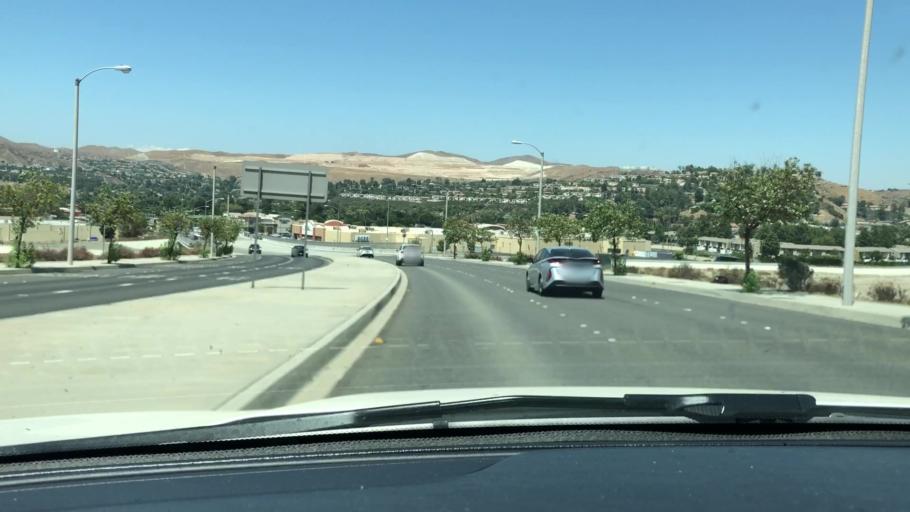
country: US
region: California
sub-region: Los Angeles County
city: Santa Clarita
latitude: 34.4112
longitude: -118.4738
